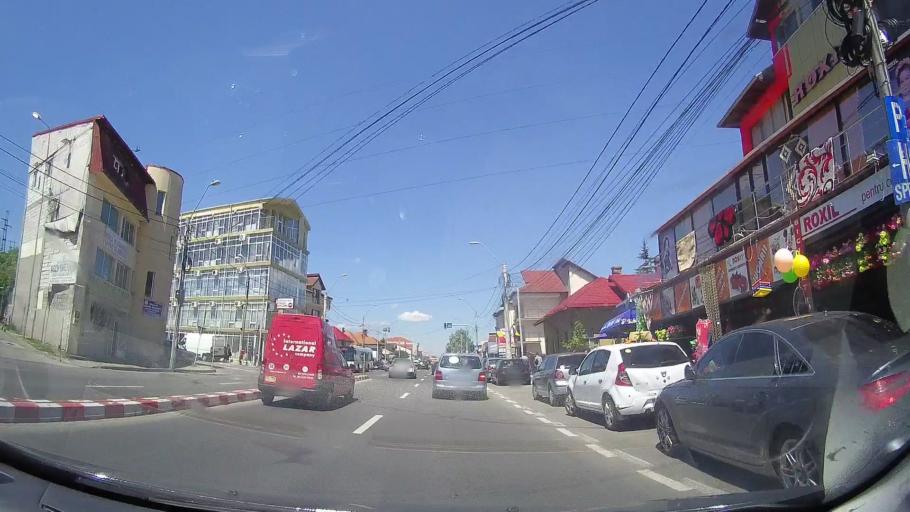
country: RO
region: Arges
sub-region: Comuna Albestii de Arges
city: Pitesti
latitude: 44.8722
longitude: 24.8516
